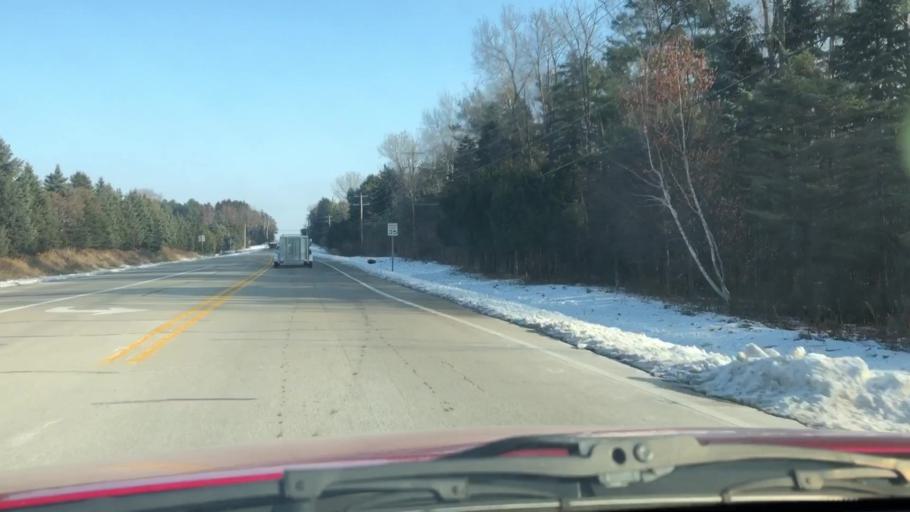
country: US
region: Wisconsin
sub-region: Outagamie County
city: Appleton
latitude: 44.3164
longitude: -88.3850
